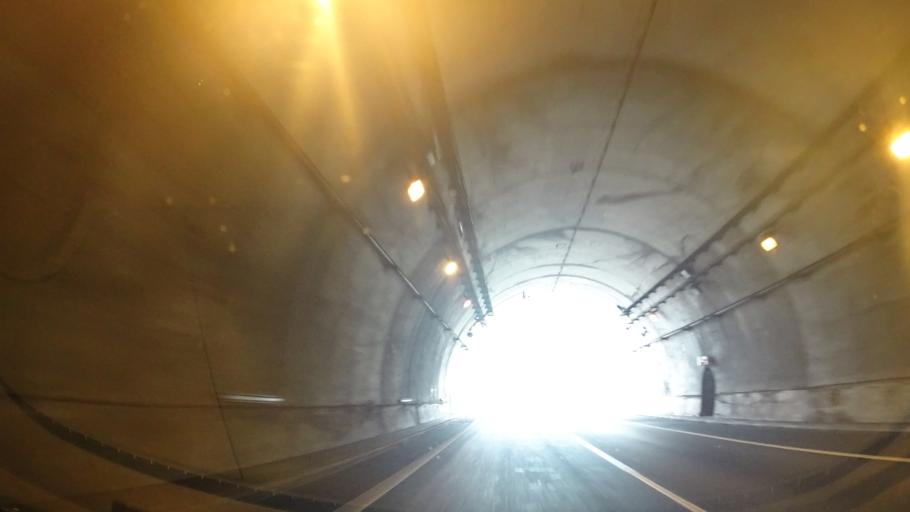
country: ES
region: Asturias
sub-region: Province of Asturias
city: Arriba
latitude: 43.4800
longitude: -5.5271
